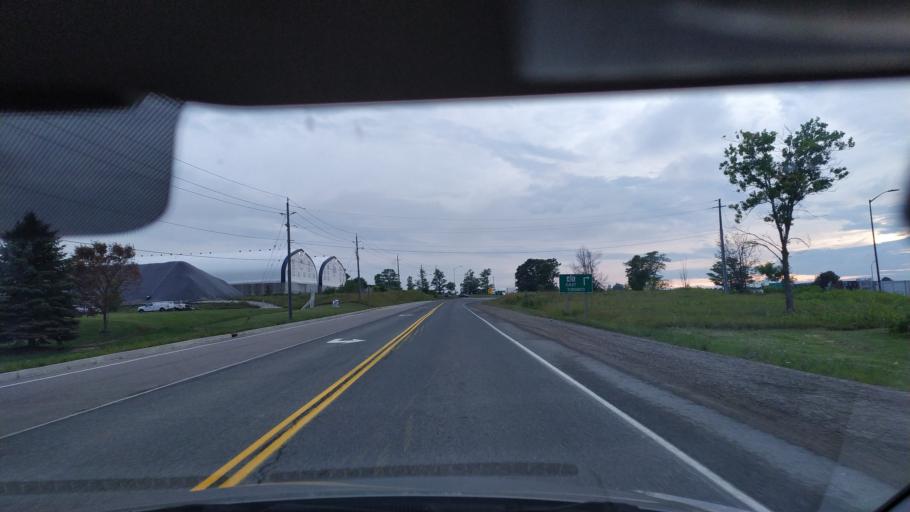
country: CA
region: Ontario
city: Kitchener
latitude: 43.3328
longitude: -80.4379
